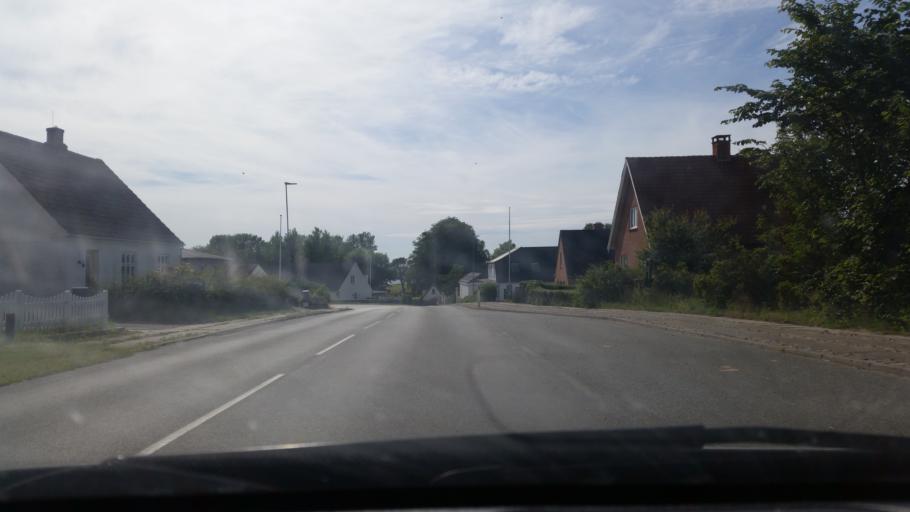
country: DK
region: Central Jutland
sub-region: Samso Kommune
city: Tranebjerg
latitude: 55.8002
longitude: 10.5367
